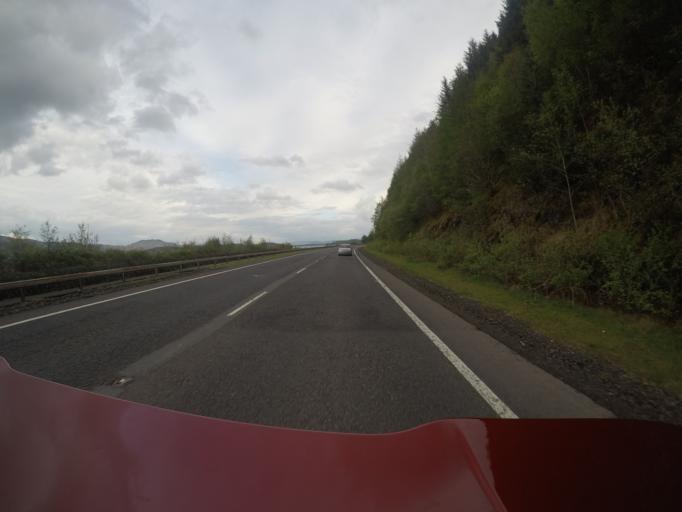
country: GB
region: Scotland
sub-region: West Dunbartonshire
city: Balloch
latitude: 56.1155
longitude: -4.6454
